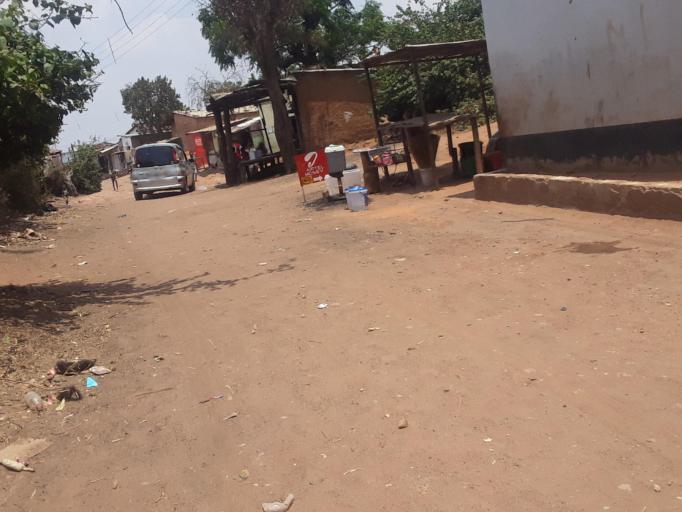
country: ZM
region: Lusaka
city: Lusaka
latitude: -15.3618
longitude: 28.3013
